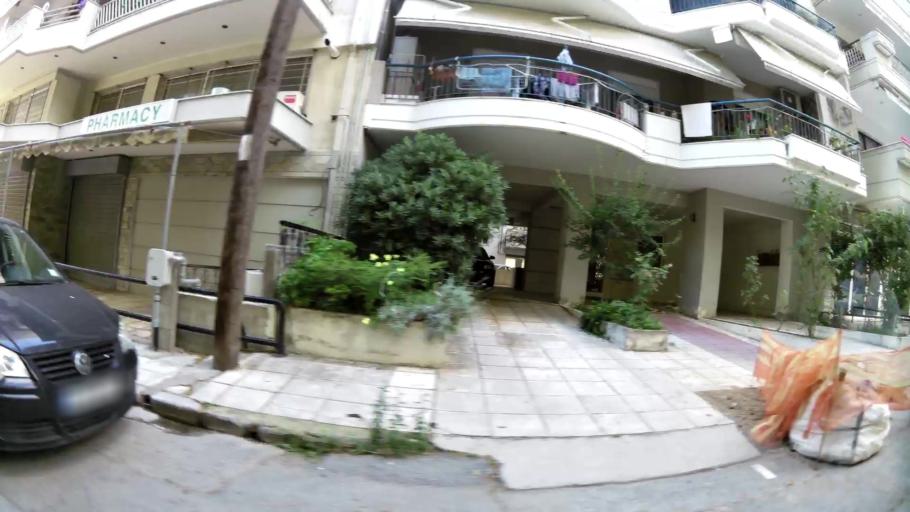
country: GR
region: Central Macedonia
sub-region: Nomos Thessalonikis
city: Kalamaria
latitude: 40.5665
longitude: 22.9603
